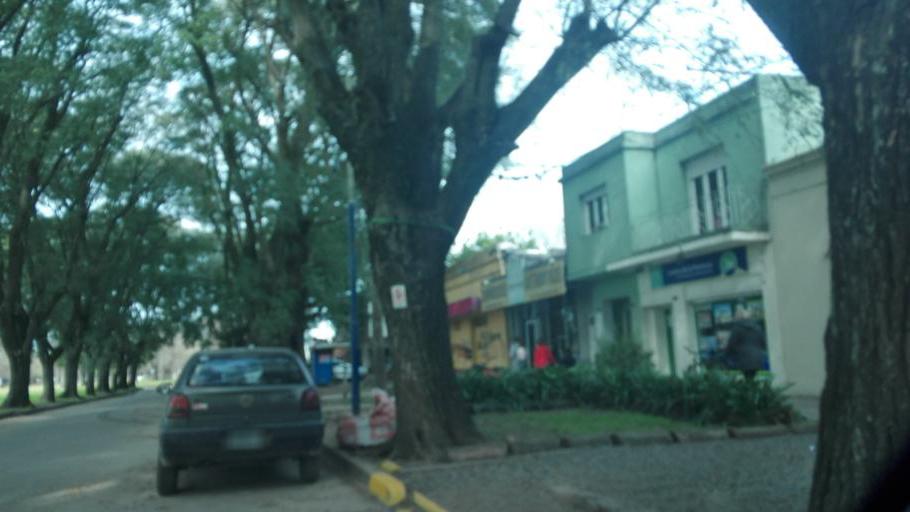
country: AR
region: Buenos Aires
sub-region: Partido de Chascomus
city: Chascomus
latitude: -35.5792
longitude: -58.0084
